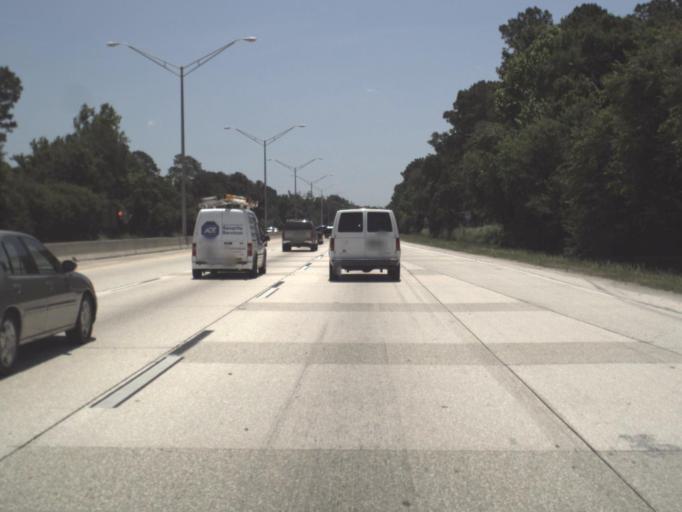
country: US
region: Florida
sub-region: Duval County
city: Jacksonville
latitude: 30.2879
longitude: -81.6270
